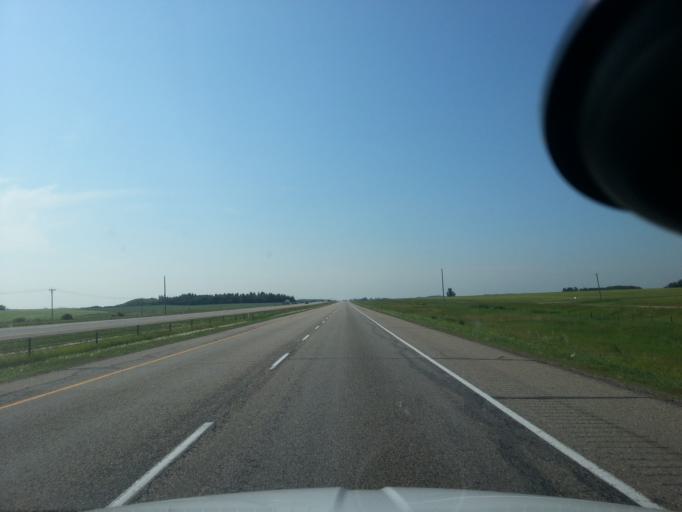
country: CA
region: Alberta
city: Olds
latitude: 51.8661
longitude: -114.0257
